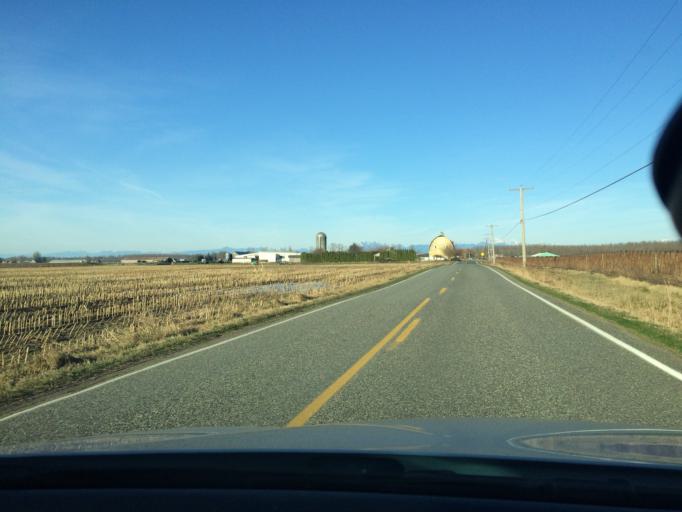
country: US
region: Washington
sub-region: Whatcom County
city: Everson
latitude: 48.9141
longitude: -122.3978
